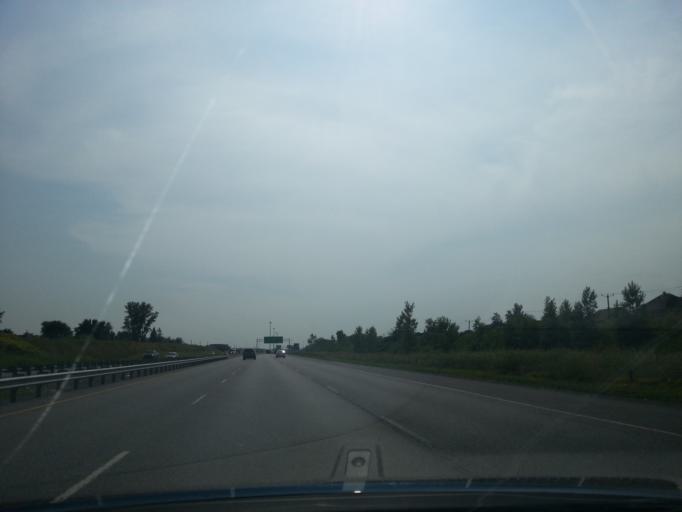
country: CA
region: Quebec
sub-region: Monteregie
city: Candiac
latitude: 45.3811
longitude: -73.4854
